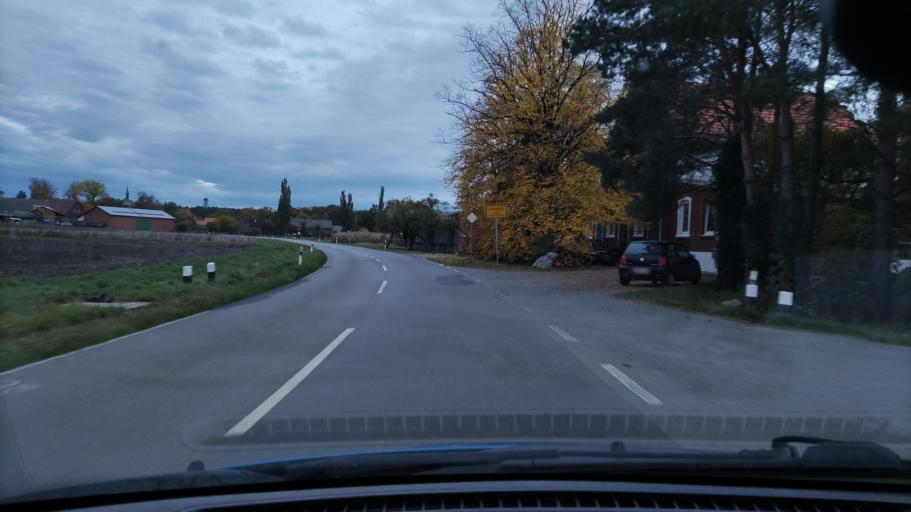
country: DE
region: Lower Saxony
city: Prezelle
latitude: 52.9583
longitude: 11.4032
